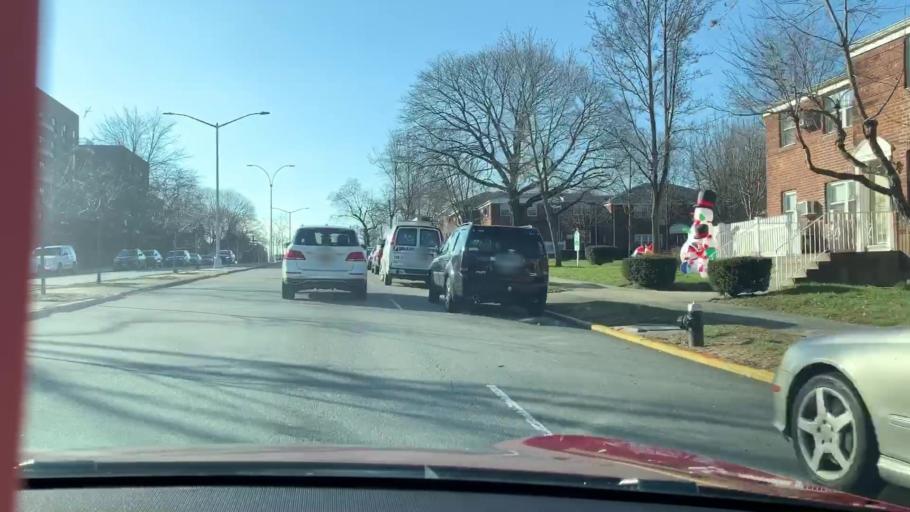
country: US
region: New York
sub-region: Nassau County
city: Bellerose Terrace
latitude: 40.7366
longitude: -73.7432
